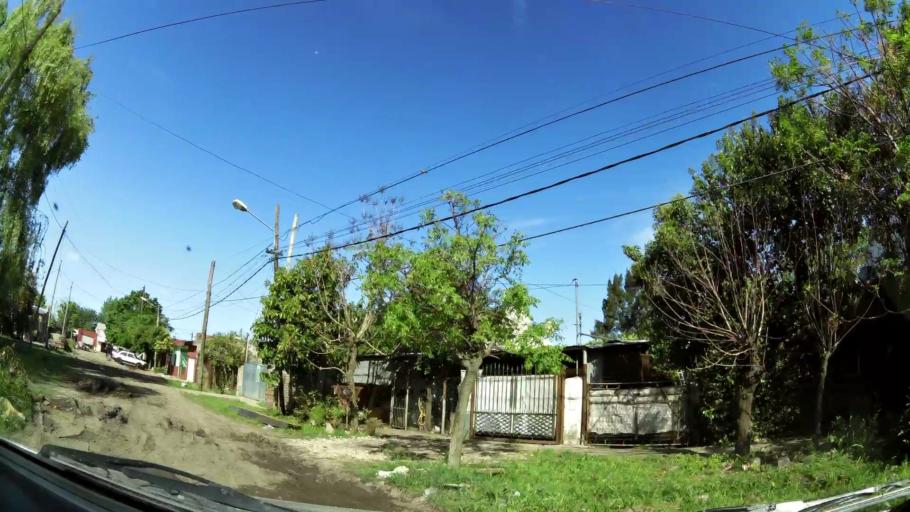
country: AR
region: Buenos Aires
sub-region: Partido de Quilmes
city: Quilmes
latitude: -34.7962
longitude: -58.2427
